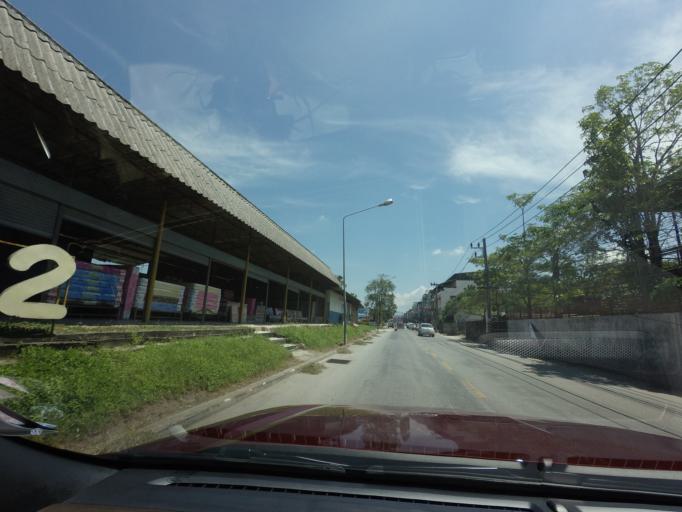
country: TH
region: Yala
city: Yala
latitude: 6.5551
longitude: 101.2832
